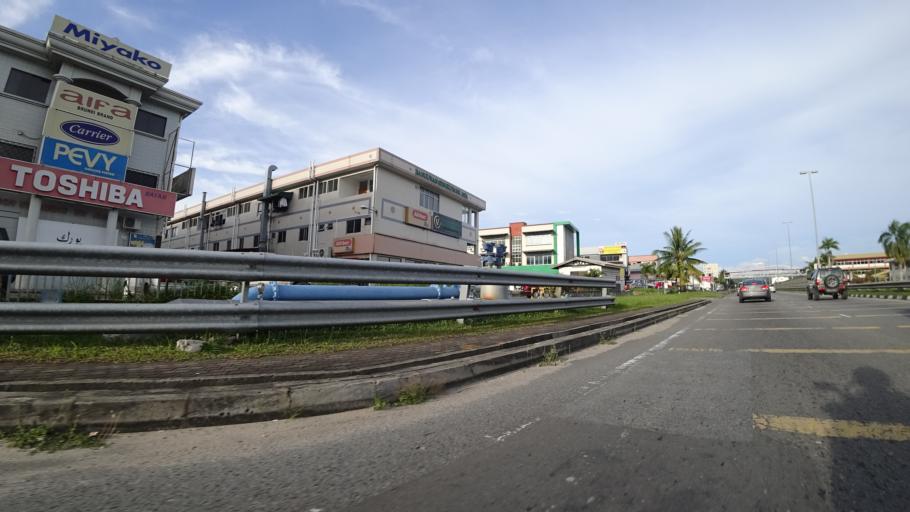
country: BN
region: Brunei and Muara
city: Bandar Seri Begawan
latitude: 4.8862
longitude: 114.8396
